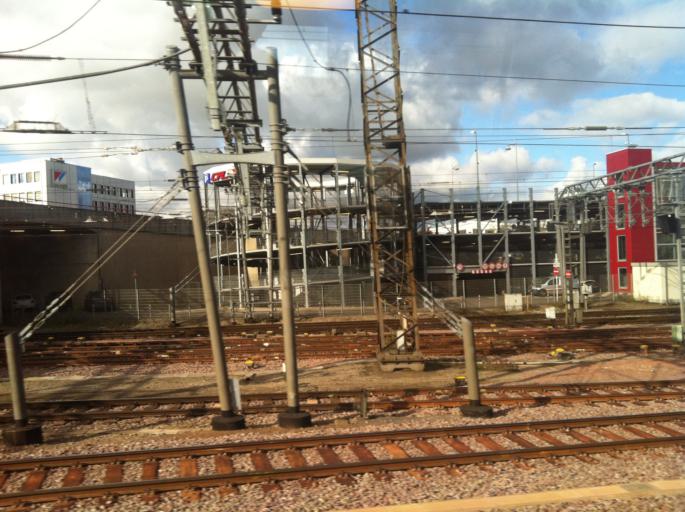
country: LU
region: Luxembourg
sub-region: Canton de Luxembourg
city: Luxembourg
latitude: 49.5962
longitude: 6.1327
